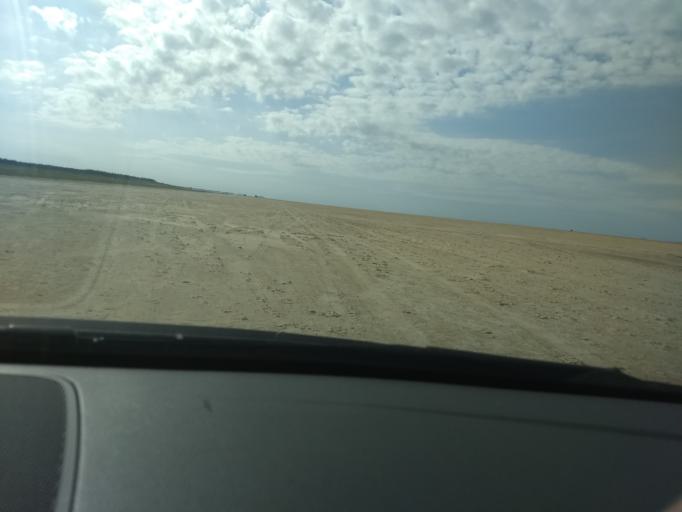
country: DE
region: Schleswig-Holstein
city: List
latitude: 55.0899
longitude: 8.5004
